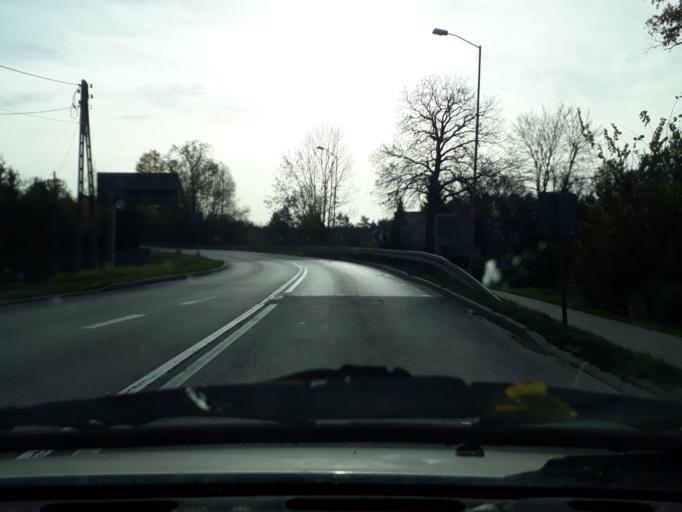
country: PL
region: Silesian Voivodeship
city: Miasteczko Slaskie
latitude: 50.5500
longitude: 18.9553
